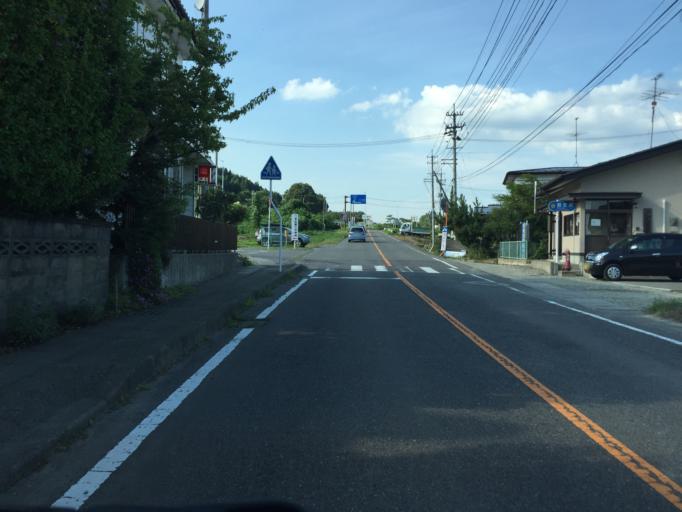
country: JP
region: Fukushima
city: Nihommatsu
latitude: 37.5670
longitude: 140.4135
